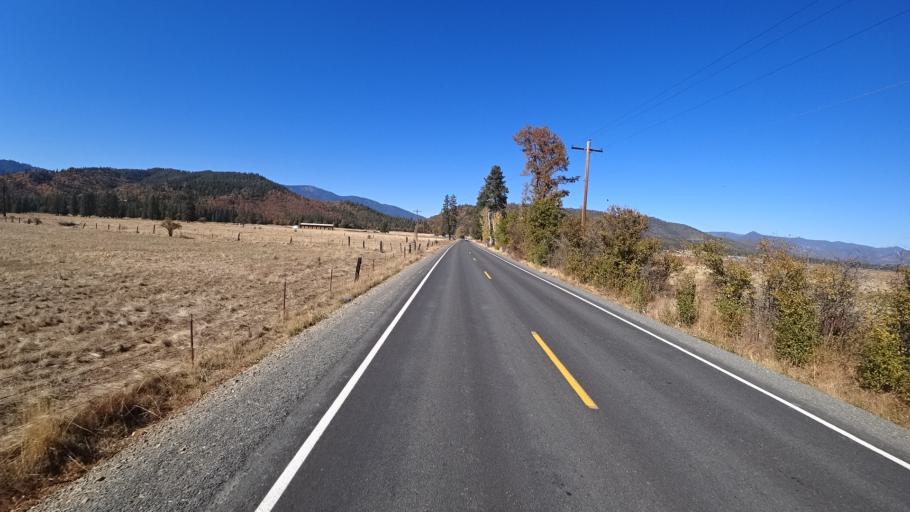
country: US
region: California
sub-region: Siskiyou County
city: Yreka
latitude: 41.5553
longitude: -122.9198
